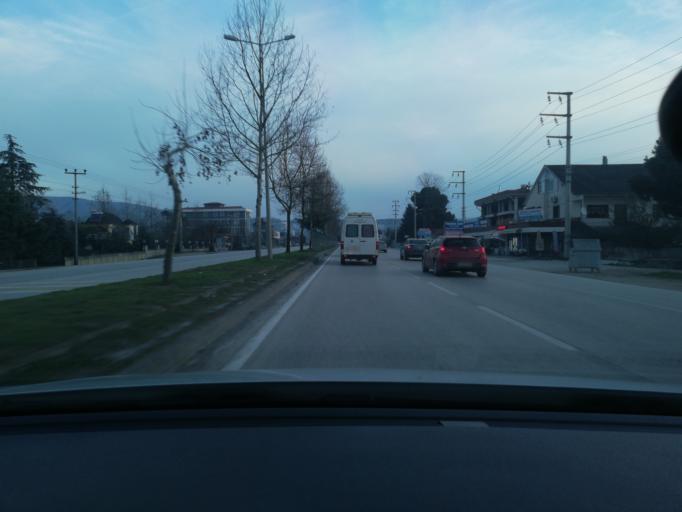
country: TR
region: Duzce
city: Konuralp
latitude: 40.8795
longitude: 31.1703
